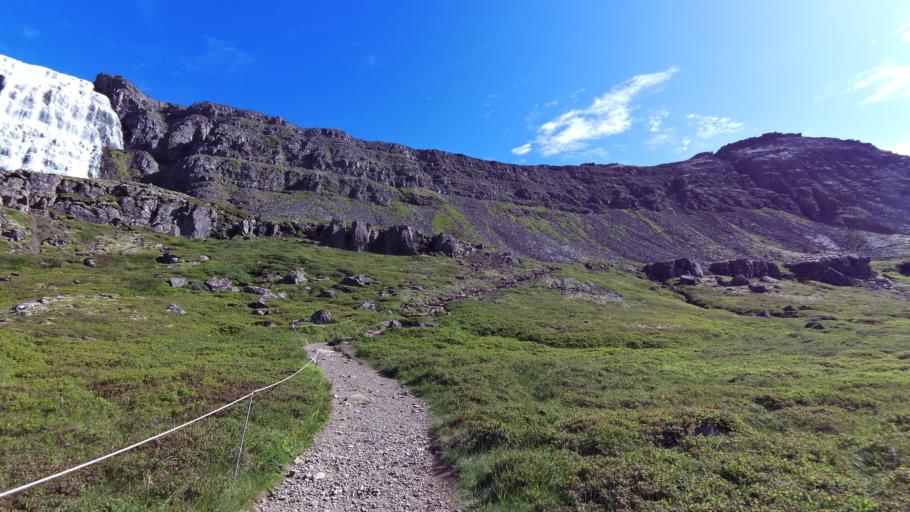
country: IS
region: Westfjords
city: Isafjoerdur
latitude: 65.7332
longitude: -23.2044
